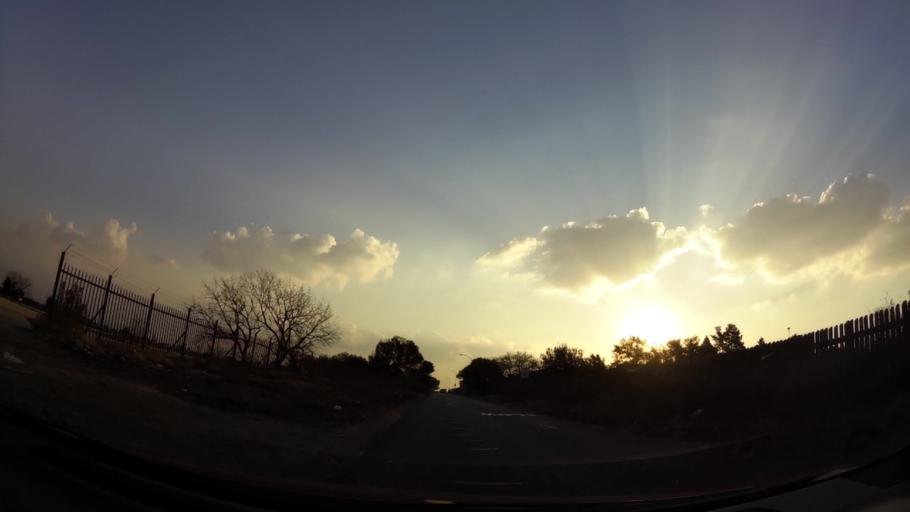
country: ZA
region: Gauteng
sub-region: City of Johannesburg Metropolitan Municipality
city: Soweto
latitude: -26.2876
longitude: 27.9047
